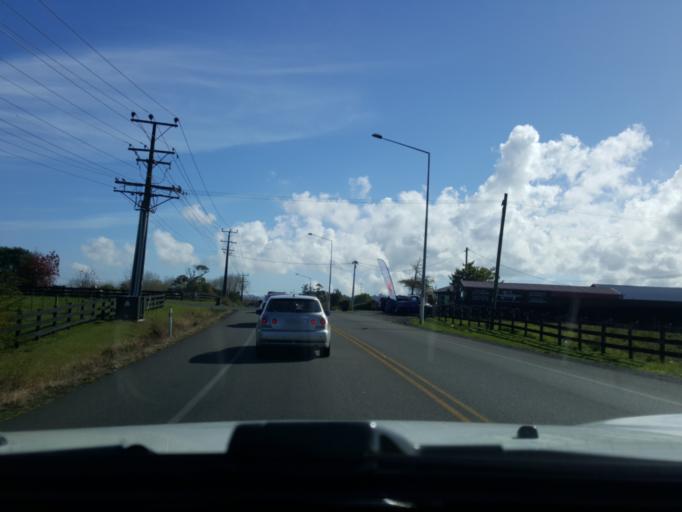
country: NZ
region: Auckland
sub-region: Auckland
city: Muriwai Beach
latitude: -36.7805
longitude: 174.5695
